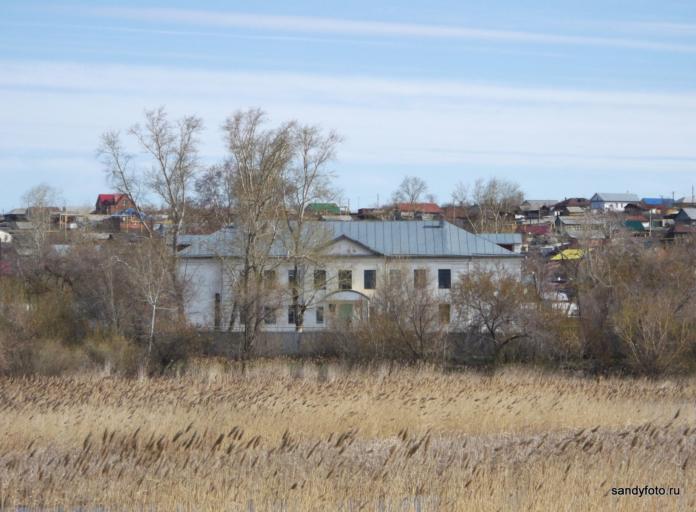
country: RU
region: Chelyabinsk
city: Troitsk
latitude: 54.0913
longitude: 61.5622
